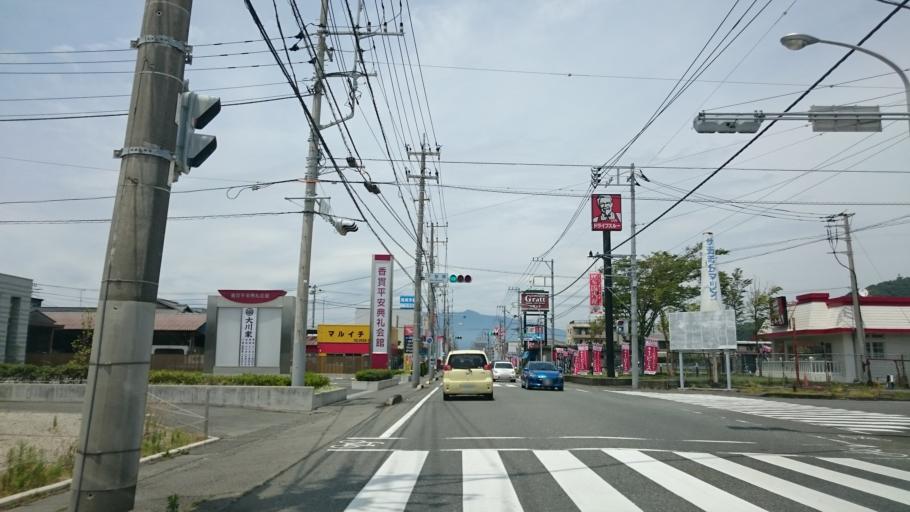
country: JP
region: Shizuoka
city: Numazu
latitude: 35.0777
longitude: 138.8717
